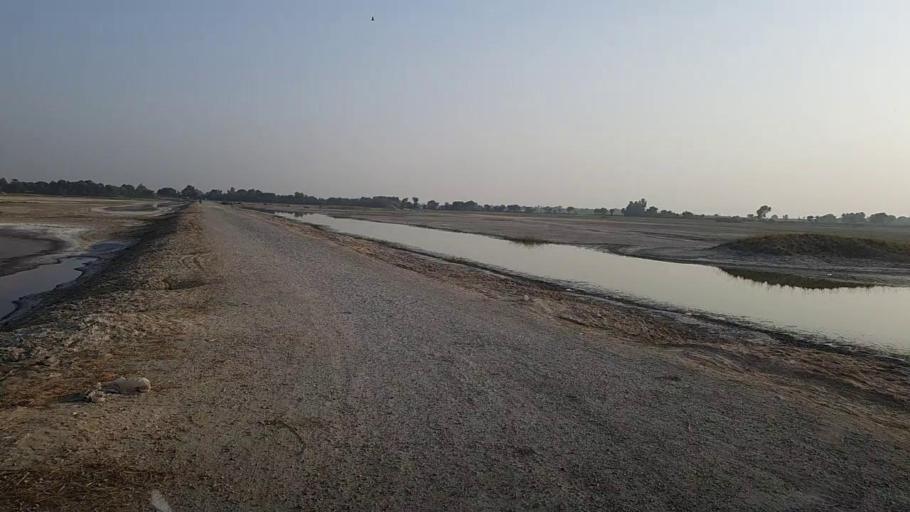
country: PK
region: Sindh
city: Kandhkot
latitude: 28.2469
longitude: 69.0904
